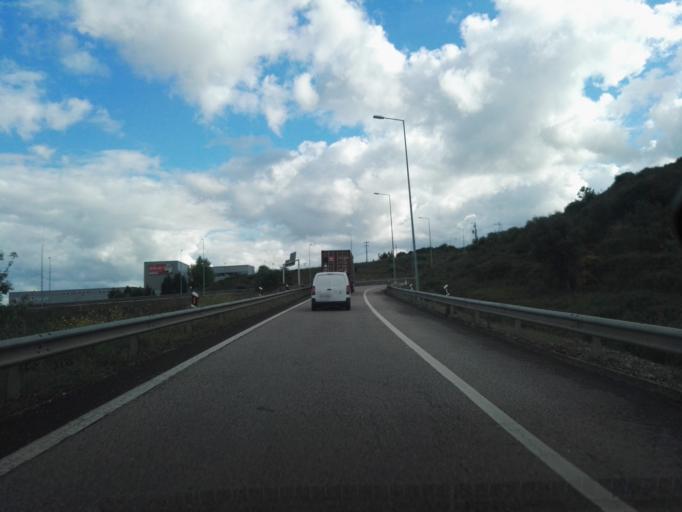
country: PT
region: Santarem
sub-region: Torres Novas
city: Torres Novas
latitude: 39.4664
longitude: -8.5332
